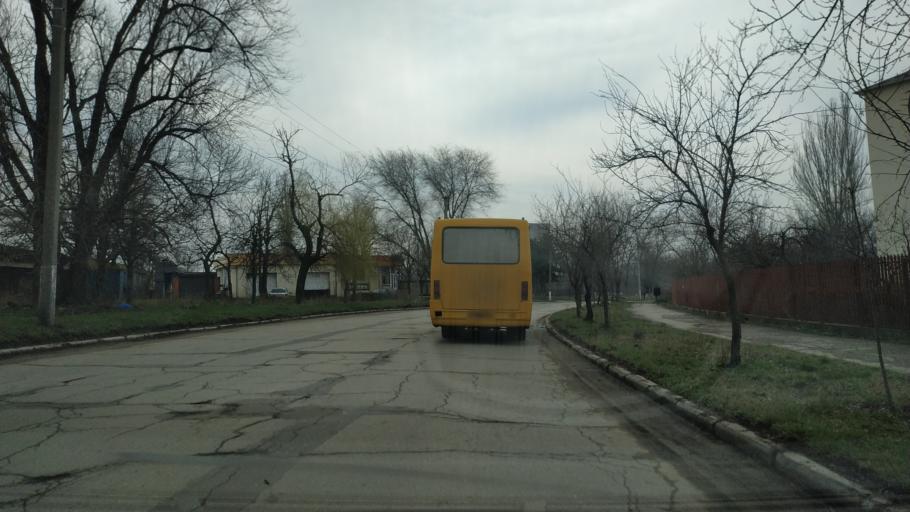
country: MD
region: Cahul
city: Cahul
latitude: 45.8926
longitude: 28.2006
